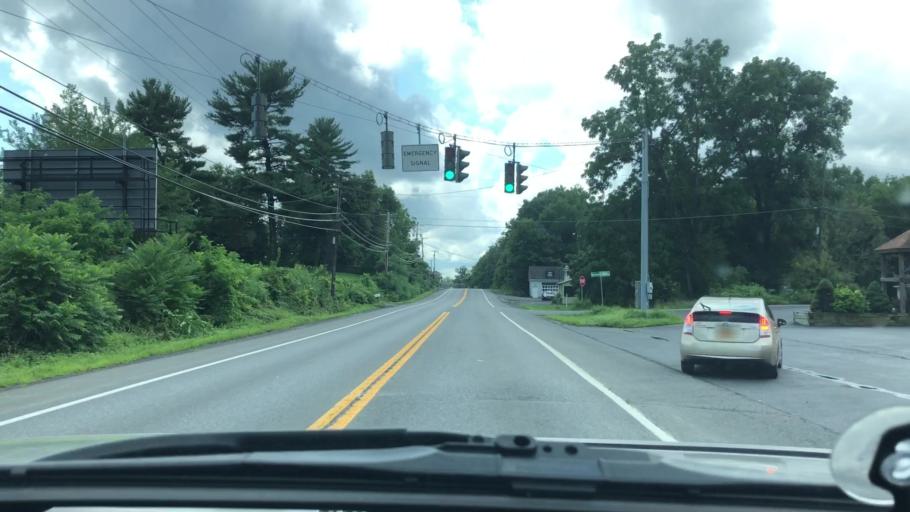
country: US
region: New York
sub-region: Ulster County
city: Saugerties
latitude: 42.0956
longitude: -73.9720
